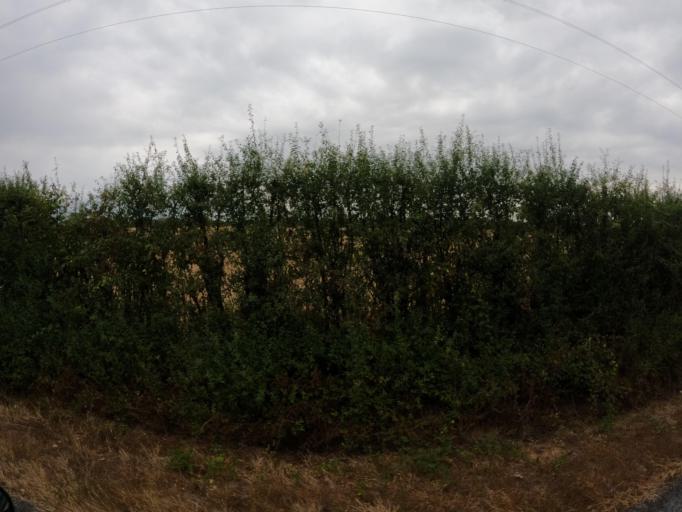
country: FR
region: Pays de la Loire
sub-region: Departement de la Vendee
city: La Boissiere-de-Montaigu
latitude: 46.9764
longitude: -1.1934
